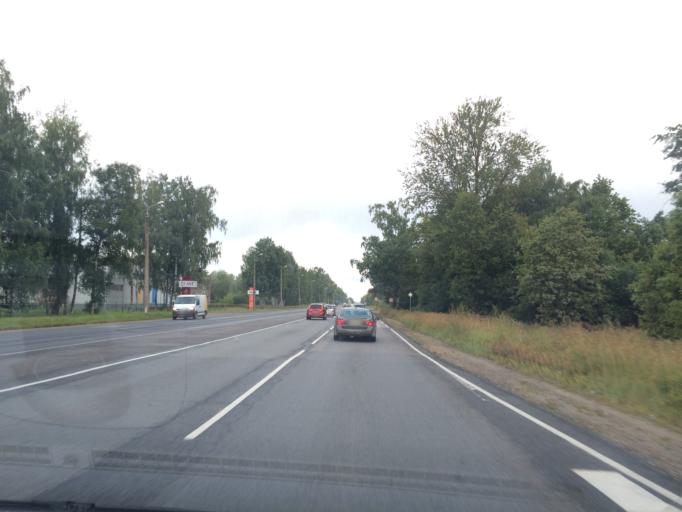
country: LV
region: Kekava
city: Kekava
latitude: 56.8789
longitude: 24.2538
